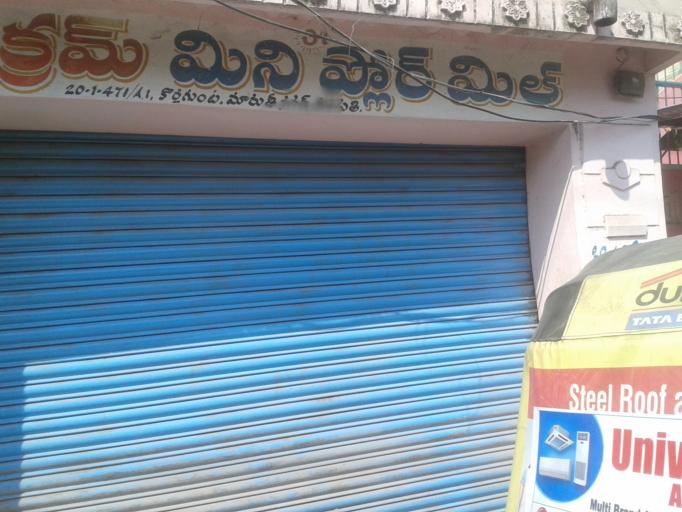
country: IN
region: Andhra Pradesh
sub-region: Chittoor
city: Tirupati
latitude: 13.6366
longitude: 79.4329
